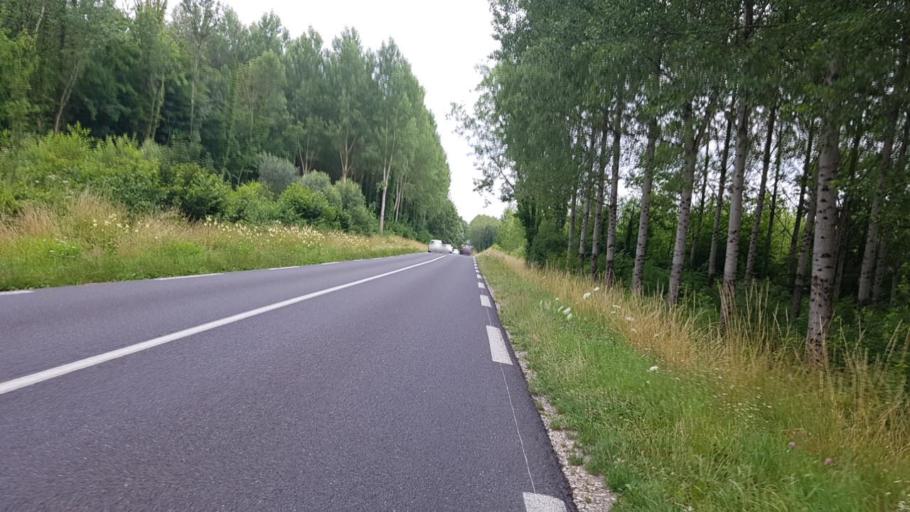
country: FR
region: Champagne-Ardenne
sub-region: Departement de la Marne
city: Sermaize-les-Bains
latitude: 48.7773
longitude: 4.8859
